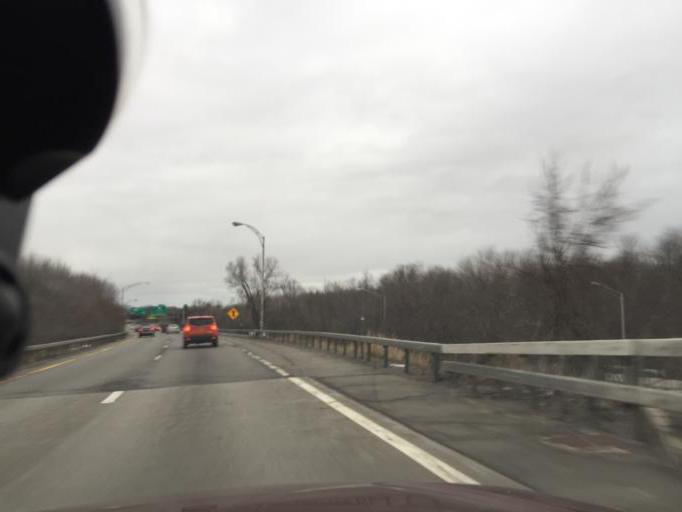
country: US
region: New York
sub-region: Monroe County
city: North Gates
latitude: 43.1584
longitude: -77.6795
